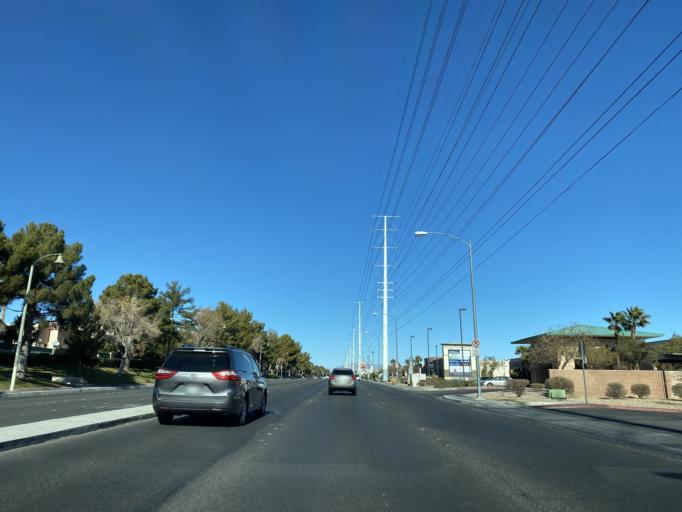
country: US
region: Nevada
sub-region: Clark County
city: Spring Valley
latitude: 36.1316
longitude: -115.2789
